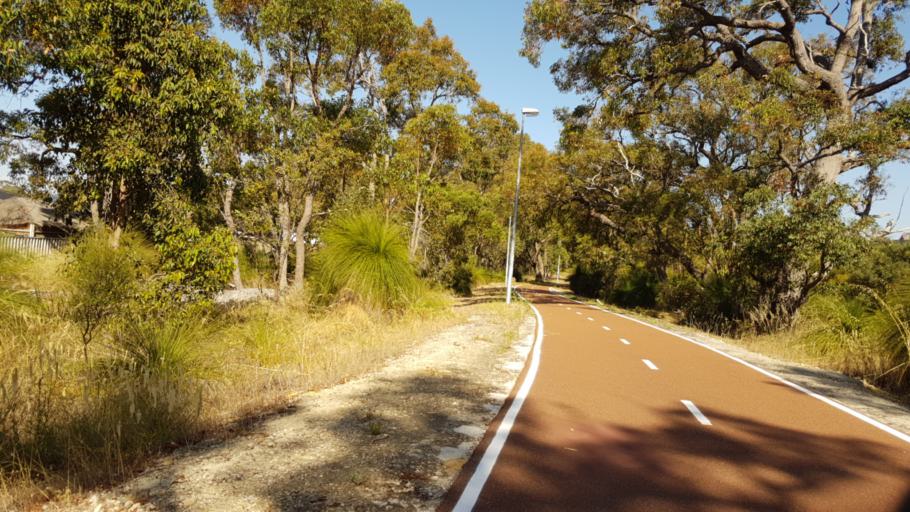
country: AU
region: Western Australia
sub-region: Stirling
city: Stirling
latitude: -31.8556
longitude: 115.8051
